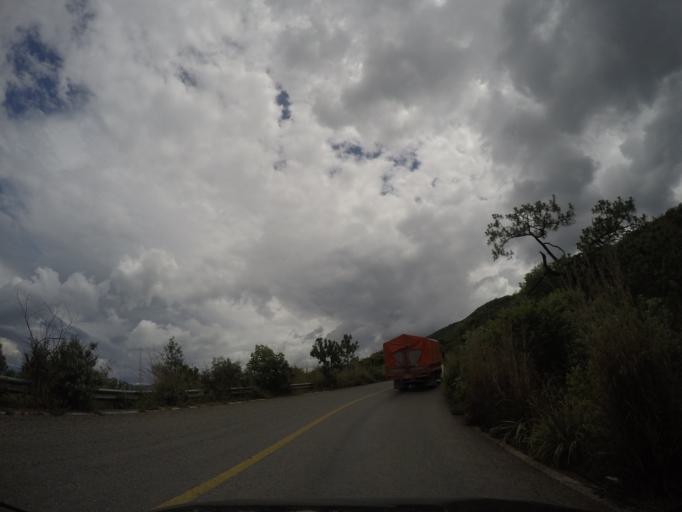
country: MX
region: Oaxaca
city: San Francisco Sola
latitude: 16.4829
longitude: -96.9799
